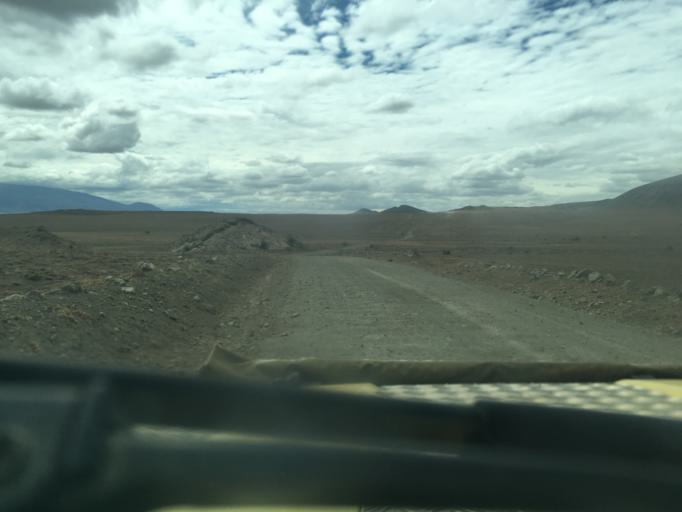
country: TZ
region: Arusha
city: Mto wa Mbu
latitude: -2.7818
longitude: 35.9893
